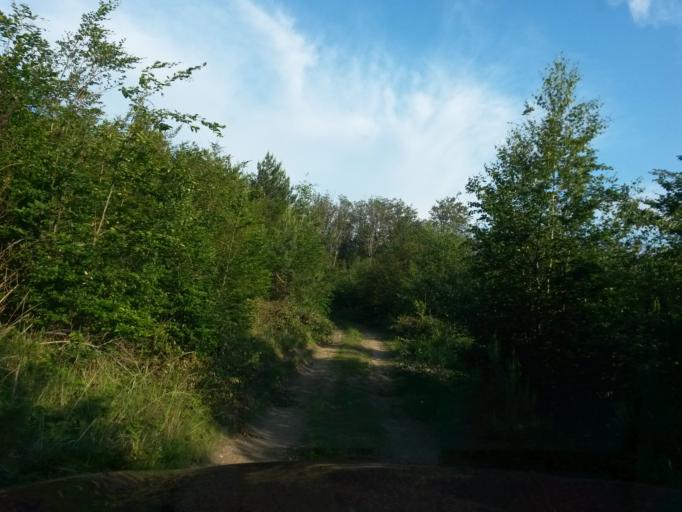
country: SK
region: Kosicky
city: Moldava nad Bodvou
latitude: 48.7373
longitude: 21.0384
